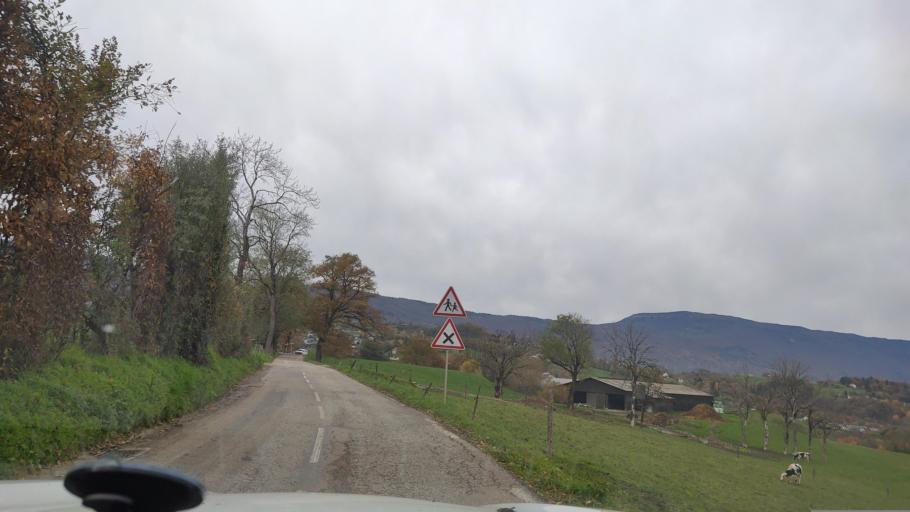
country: FR
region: Rhone-Alpes
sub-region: Departement de la Savoie
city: Jacob-Bellecombette
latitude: 45.5434
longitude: 5.8950
